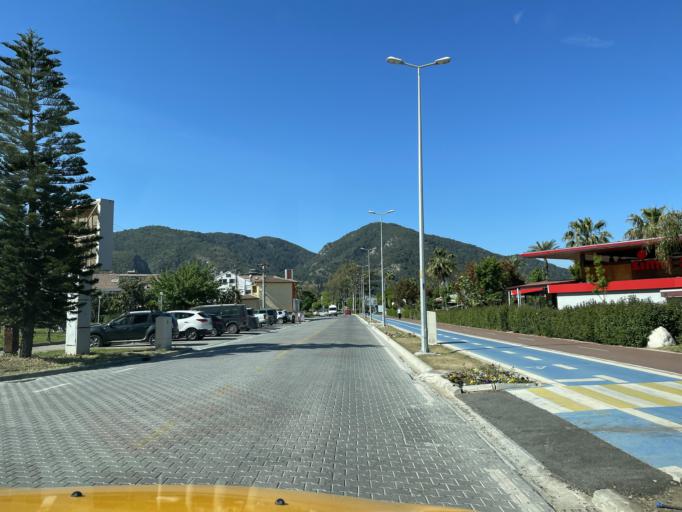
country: TR
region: Mugla
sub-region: Fethiye
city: Fethiye
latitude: 36.6320
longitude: 29.1192
